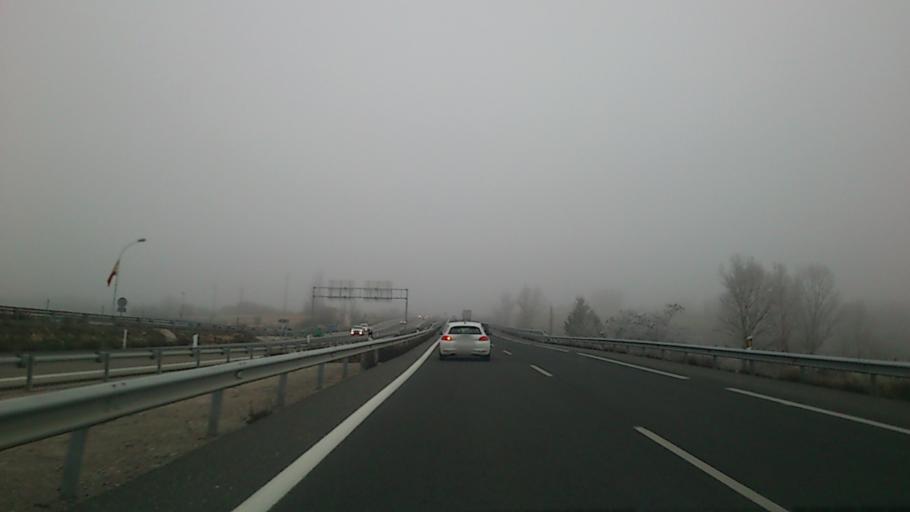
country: ES
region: Castille-La Mancha
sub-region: Provincia de Guadalajara
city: Almadrones
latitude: 40.8996
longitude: -2.7554
